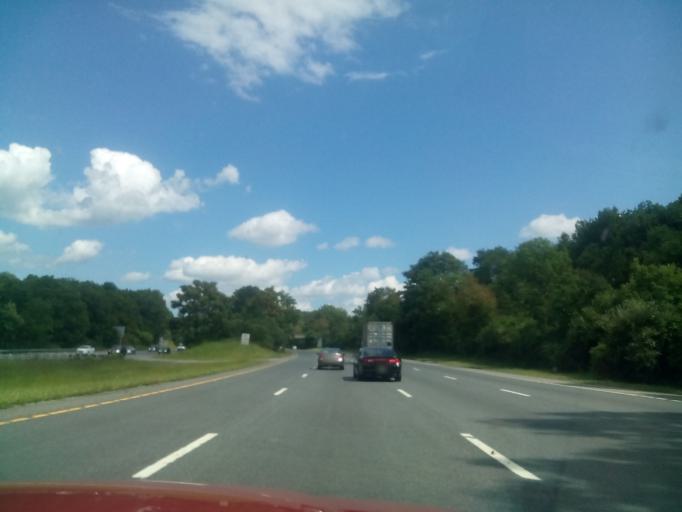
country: US
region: New Jersey
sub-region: Warren County
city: Belvidere
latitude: 40.9225
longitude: -75.0625
